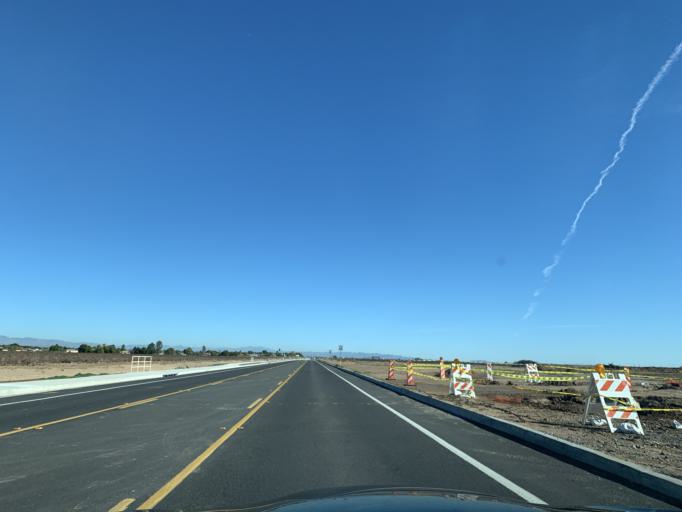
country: US
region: Arizona
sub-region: Maricopa County
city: Queen Creek
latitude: 33.2195
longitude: -111.6174
